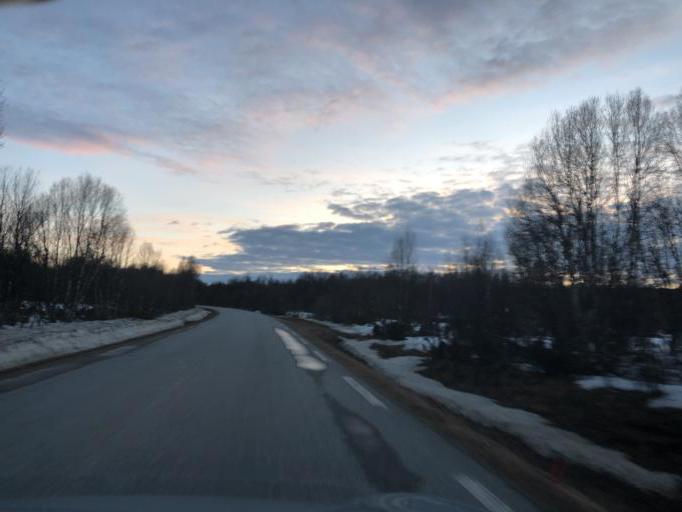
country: NO
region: Sor-Trondelag
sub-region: Tydal
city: Aas
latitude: 62.6781
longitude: 11.8525
